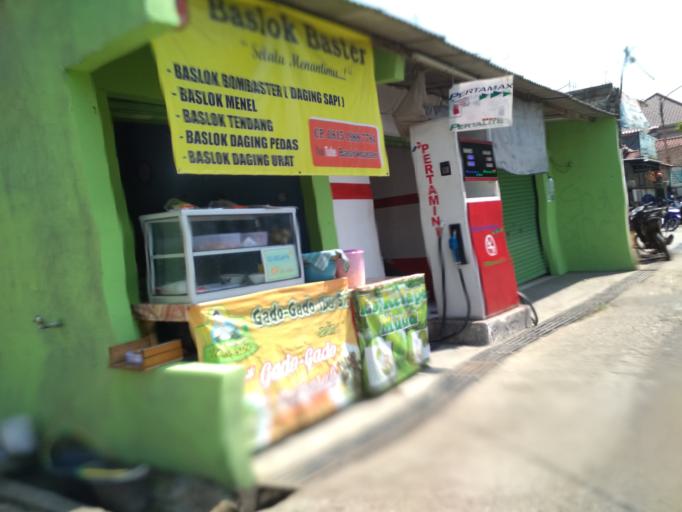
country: ID
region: West Java
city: Ciampea
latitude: -6.5559
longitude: 106.7483
